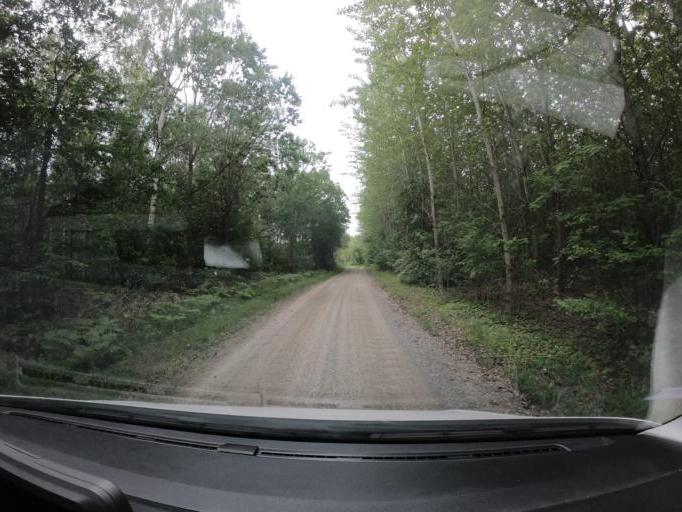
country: SE
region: Skane
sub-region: Perstorps Kommun
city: Perstorp
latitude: 56.1941
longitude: 13.5244
